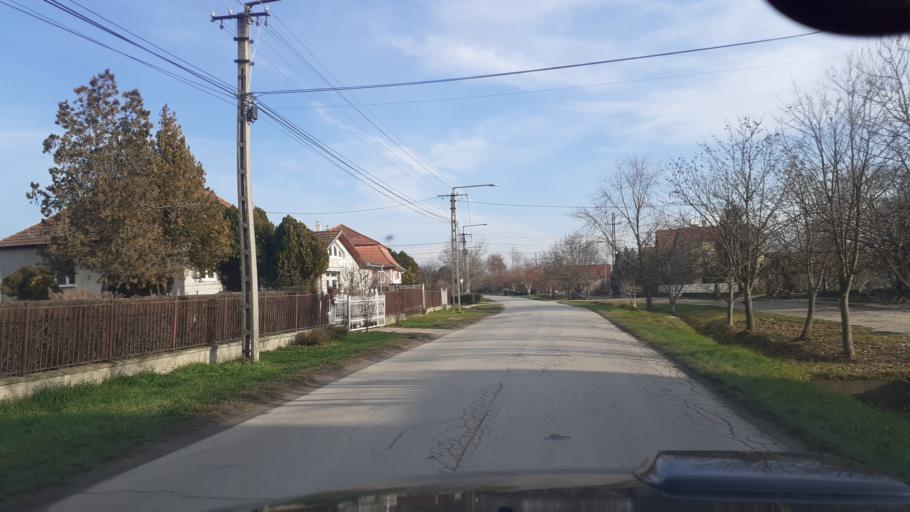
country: HU
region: Pest
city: Domsod
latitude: 47.0927
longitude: 19.0147
